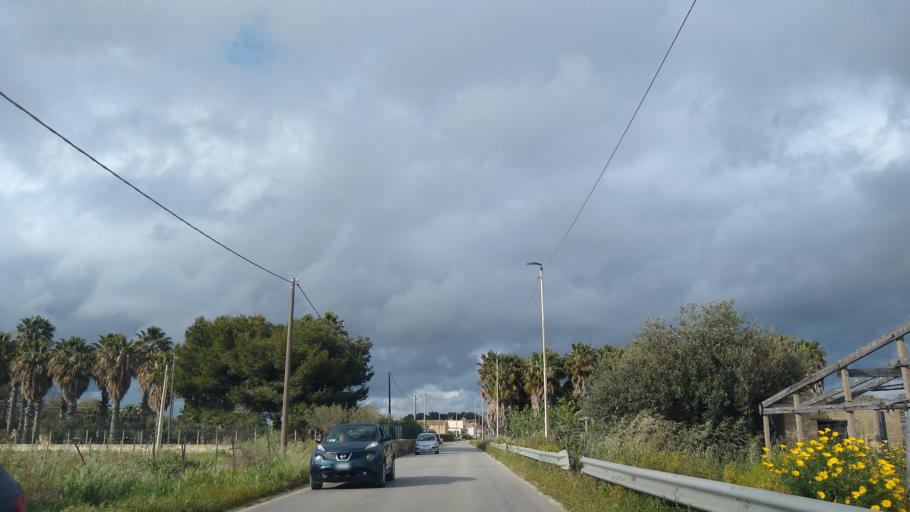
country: IT
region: Sicily
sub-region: Trapani
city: Marsala
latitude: 37.8523
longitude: 12.4850
